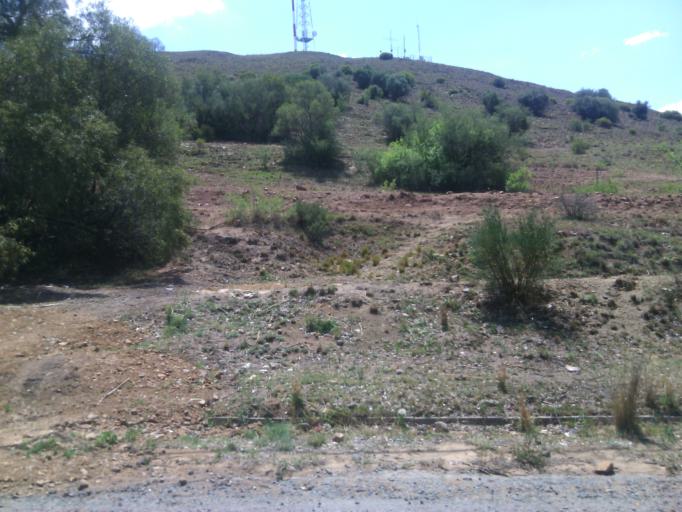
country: ZA
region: Orange Free State
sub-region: Xhariep District Municipality
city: Dewetsdorp
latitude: -29.5814
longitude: 26.6606
